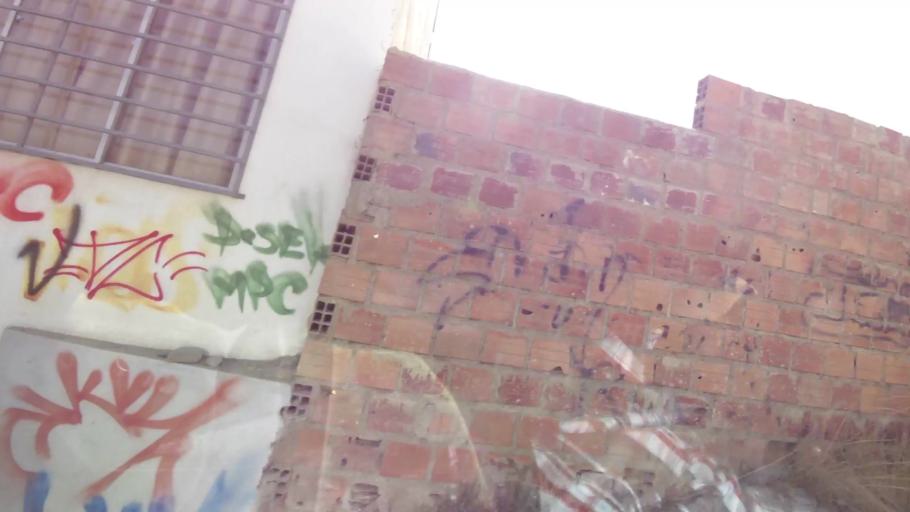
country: BO
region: La Paz
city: La Paz
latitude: -16.5401
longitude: -68.0470
